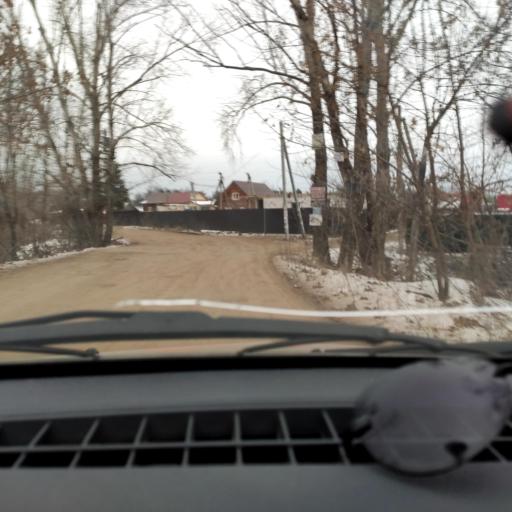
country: RU
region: Bashkortostan
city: Ufa
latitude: 54.7694
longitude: 55.9377
